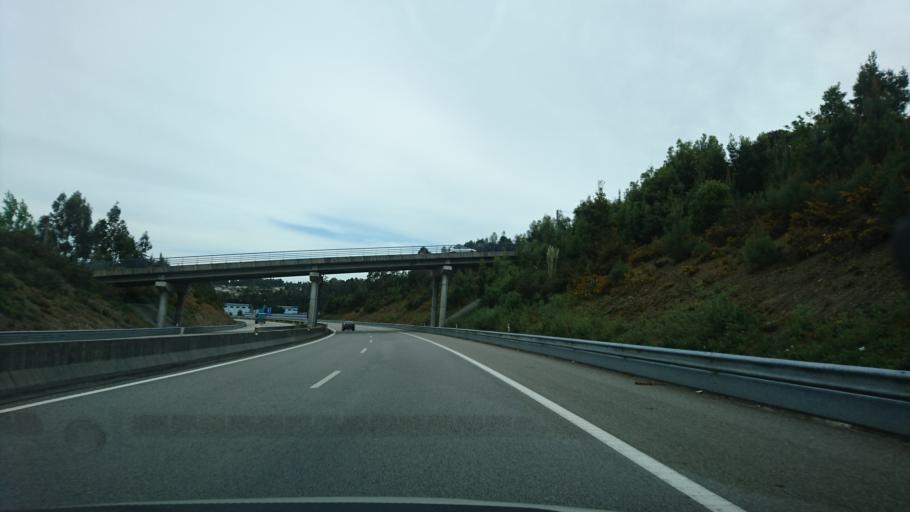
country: PT
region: Aveiro
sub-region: Santa Maria da Feira
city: Argoncilhe
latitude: 41.0098
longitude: -8.5353
